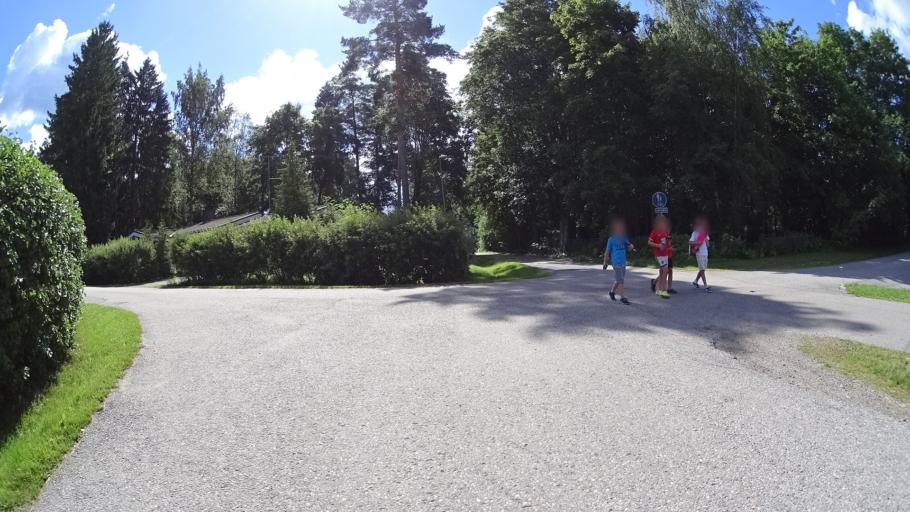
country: FI
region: Uusimaa
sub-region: Helsinki
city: Tuusula
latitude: 60.3922
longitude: 25.0248
